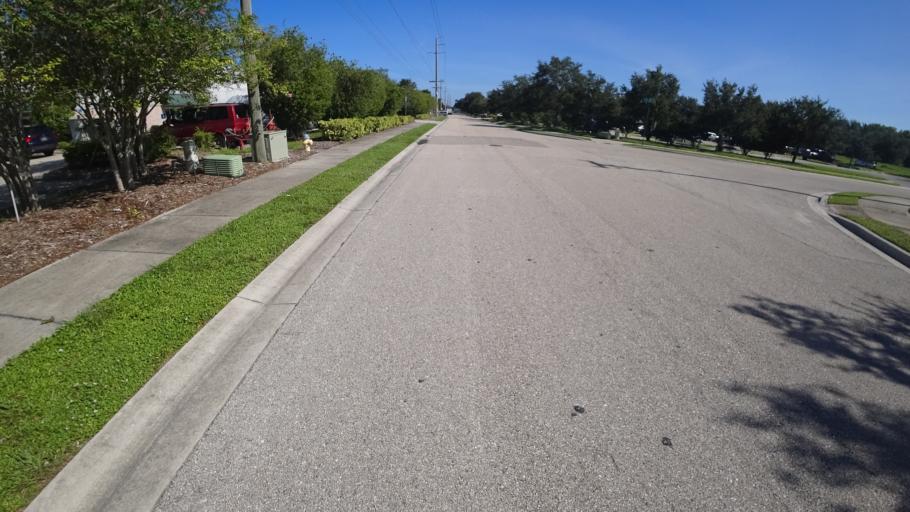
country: US
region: Florida
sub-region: Manatee County
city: Whitfield
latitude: 27.4127
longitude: -82.5386
